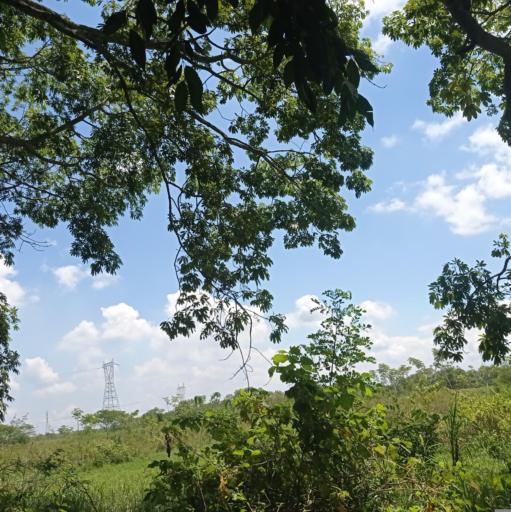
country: CO
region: Santander
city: Barrancabermeja
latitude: 7.0986
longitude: -73.8781
